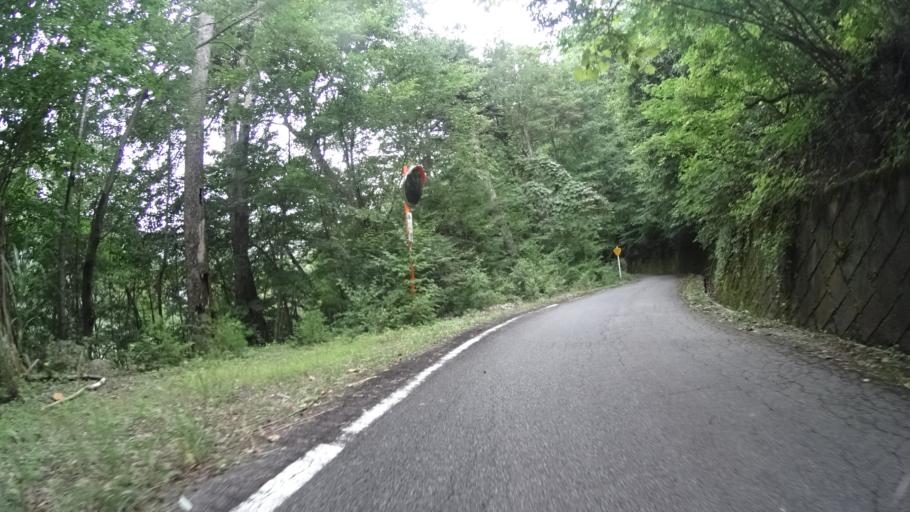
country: JP
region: Yamanashi
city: Kofu-shi
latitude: 35.8088
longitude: 138.6033
